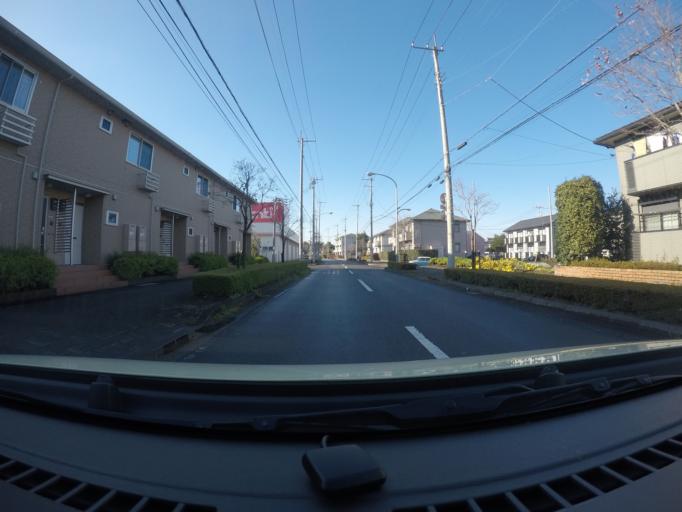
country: JP
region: Ibaraki
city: Tsukuba
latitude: 36.1304
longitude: 140.0815
